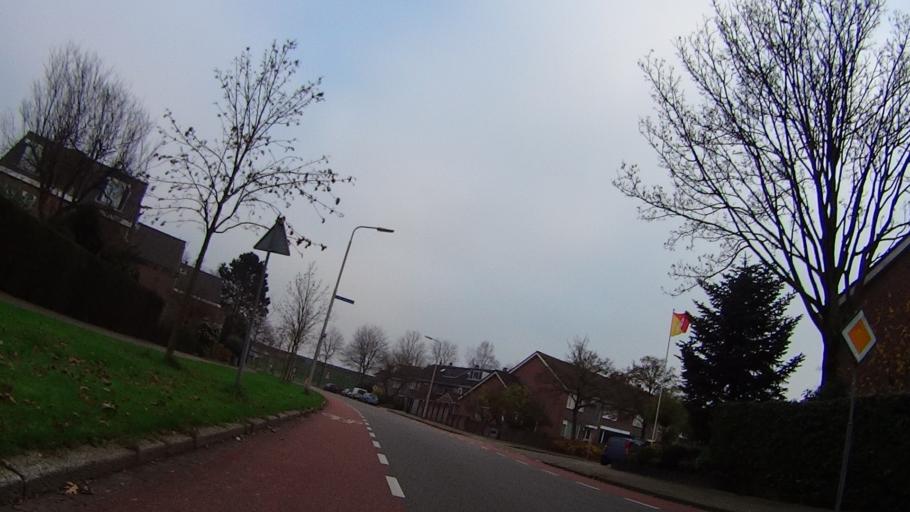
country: NL
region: Utrecht
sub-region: Gemeente Amersfoort
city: Randenbroek
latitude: 52.1659
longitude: 5.4178
